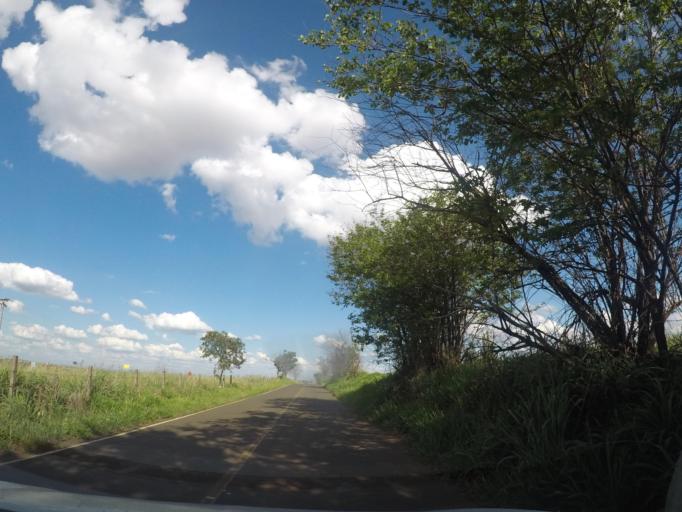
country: BR
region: Sao Paulo
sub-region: Sumare
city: Sumare
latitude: -22.8544
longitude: -47.3203
